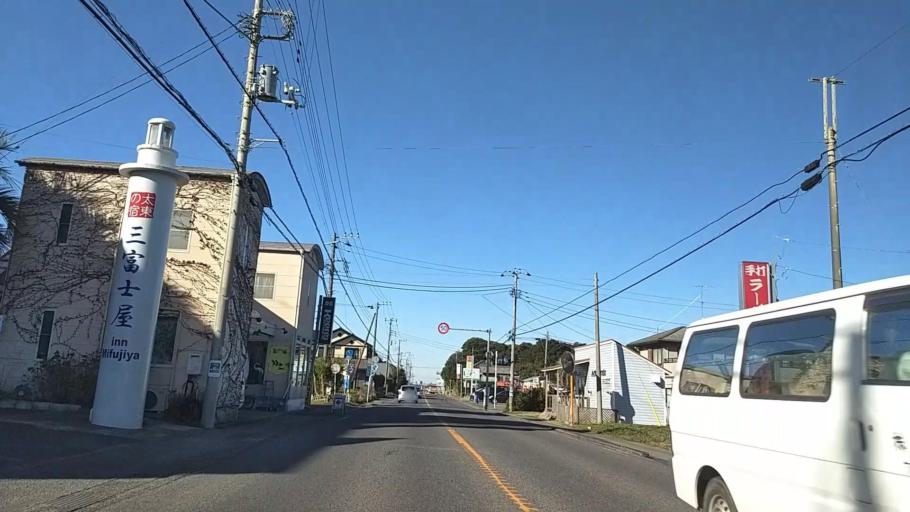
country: JP
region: Chiba
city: Ohara
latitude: 35.3275
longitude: 140.3981
